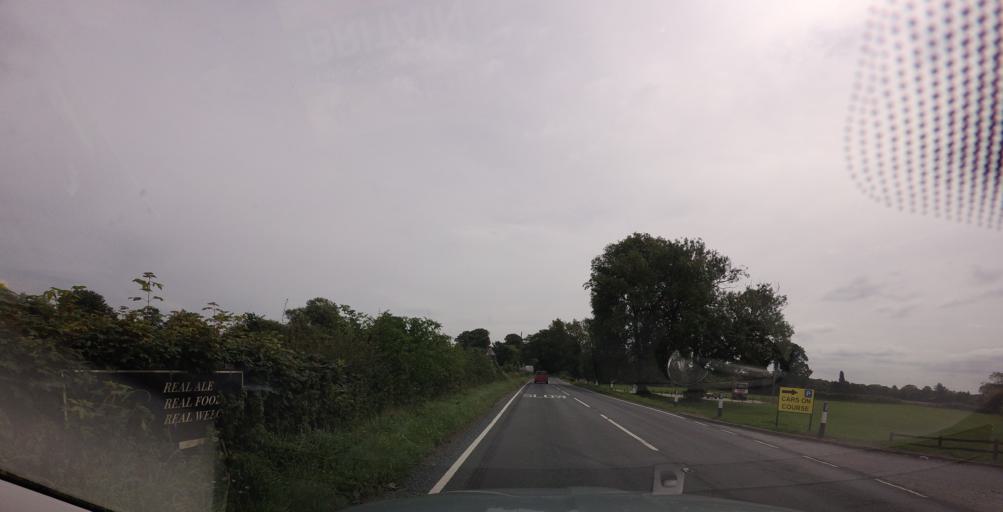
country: GB
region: England
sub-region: North Yorkshire
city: Ripon
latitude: 54.1265
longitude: -1.4957
